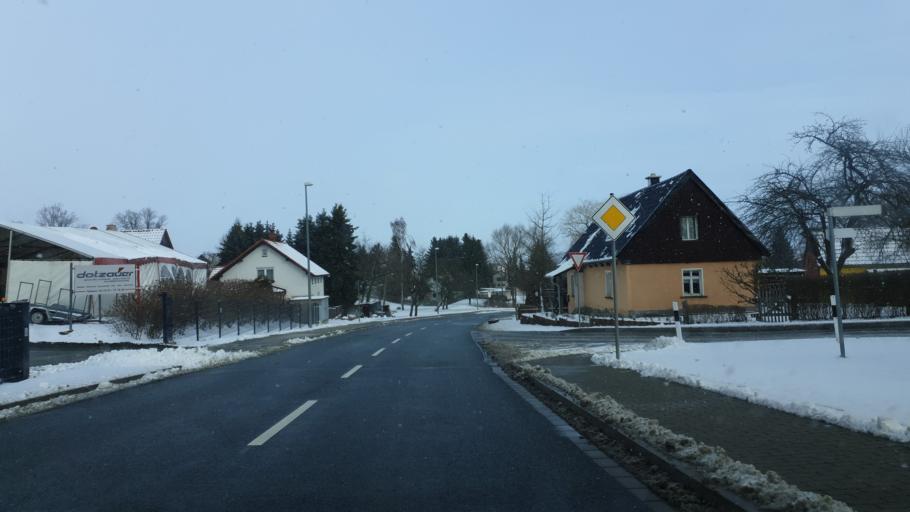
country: DE
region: Saxony
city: Oelsnitz
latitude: 50.3936
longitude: 12.1503
